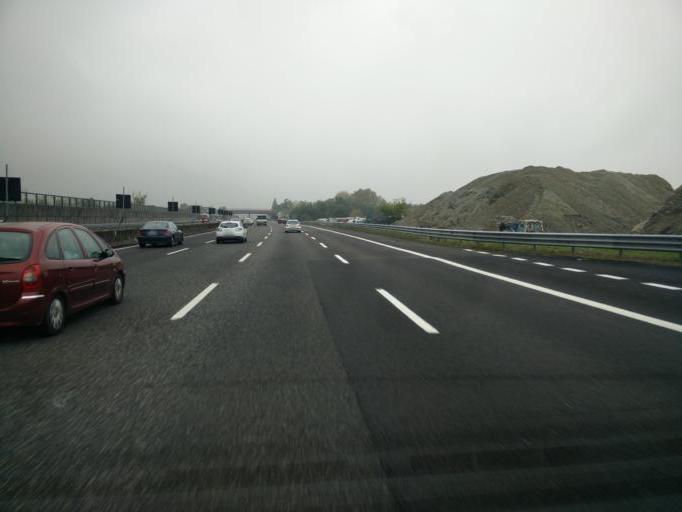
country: IT
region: Emilia-Romagna
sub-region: Provincia di Modena
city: San Cesario sul Panaro
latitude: 44.5652
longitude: 11.0428
